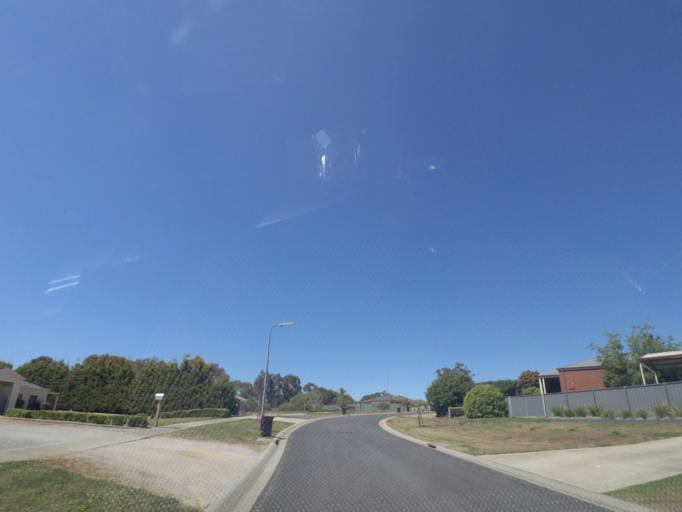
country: AU
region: Victoria
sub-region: Whittlesea
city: Whittlesea
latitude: -37.2084
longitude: 145.0640
